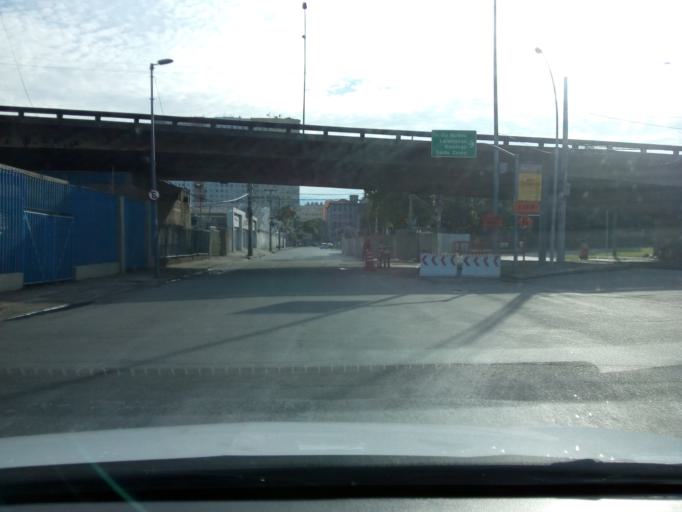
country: BR
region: Rio de Janeiro
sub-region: Rio De Janeiro
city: Rio de Janeiro
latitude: -22.9084
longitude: -43.1975
